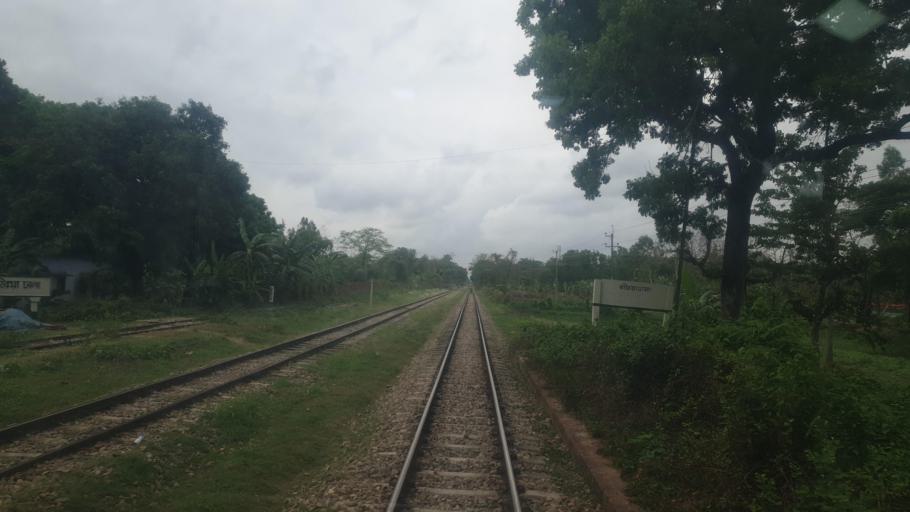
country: BD
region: Chittagong
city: Fatikchari
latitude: 22.6785
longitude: 91.6340
